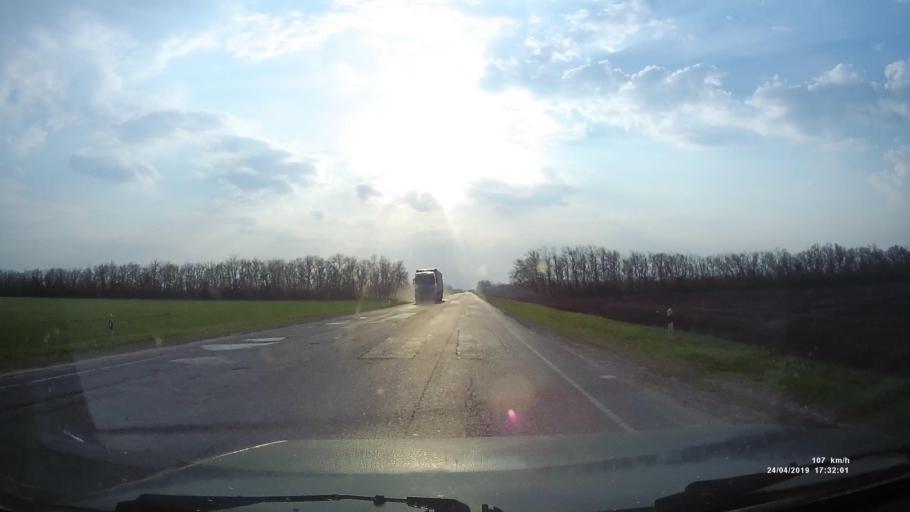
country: RU
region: Rostov
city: Tselina
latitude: 46.5248
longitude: 41.1072
